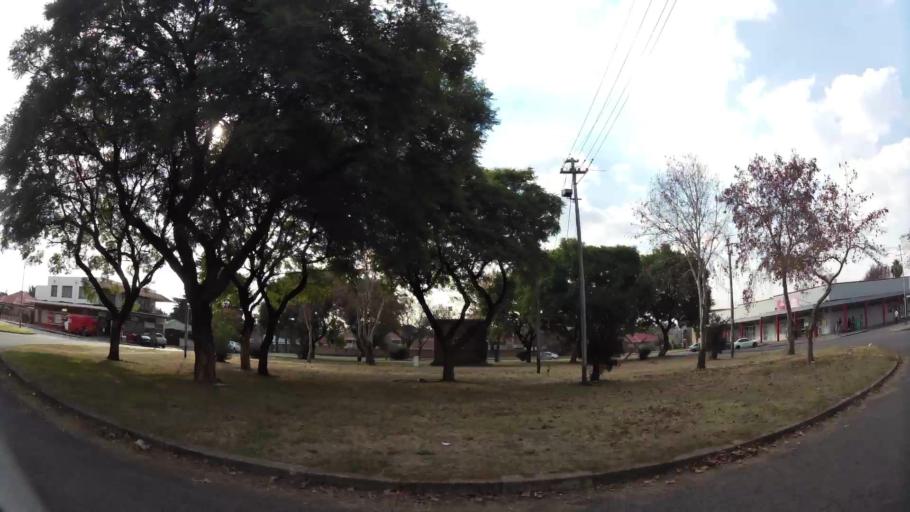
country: ZA
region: Gauteng
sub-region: Ekurhuleni Metropolitan Municipality
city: Germiston
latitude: -26.2317
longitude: 28.1749
